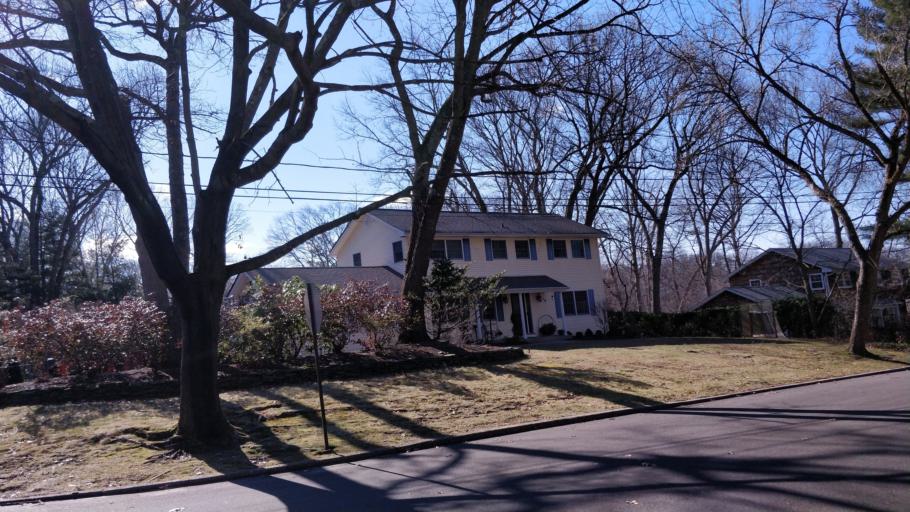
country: US
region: New York
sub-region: Suffolk County
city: Setauket-East Setauket
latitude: 40.9282
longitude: -73.1056
